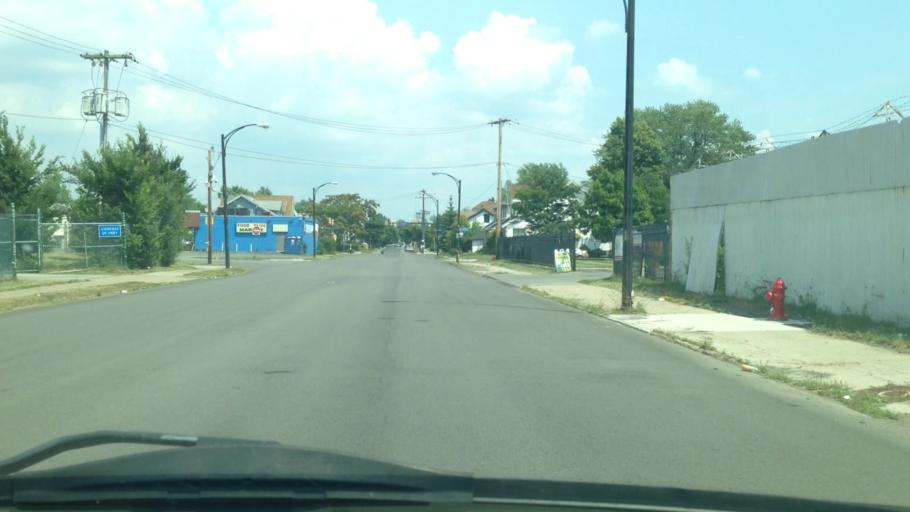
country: US
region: New York
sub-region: Erie County
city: Eggertsville
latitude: 42.9401
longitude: -78.8238
